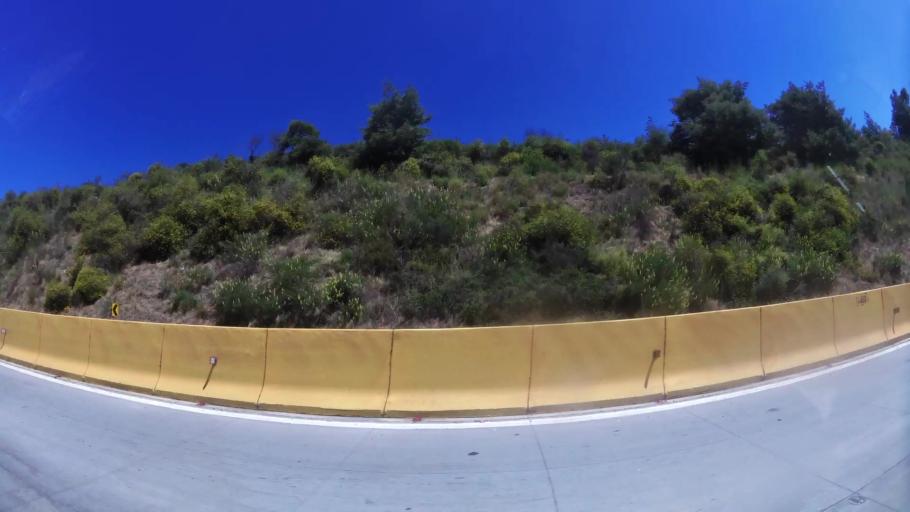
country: CL
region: Valparaiso
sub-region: Provincia de Valparaiso
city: Valparaiso
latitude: -33.0671
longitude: -71.6412
